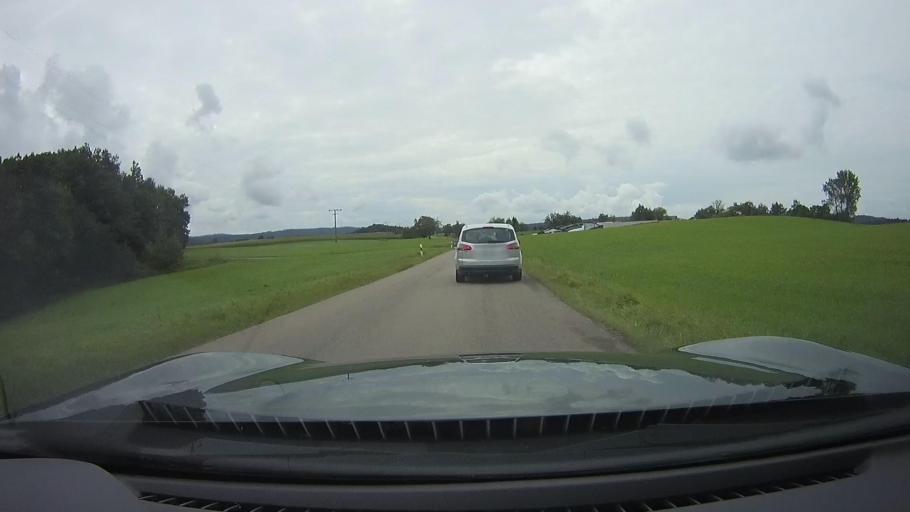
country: DE
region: Baden-Wuerttemberg
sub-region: Regierungsbezirk Stuttgart
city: Murrhardt
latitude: 49.0105
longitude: 9.5651
